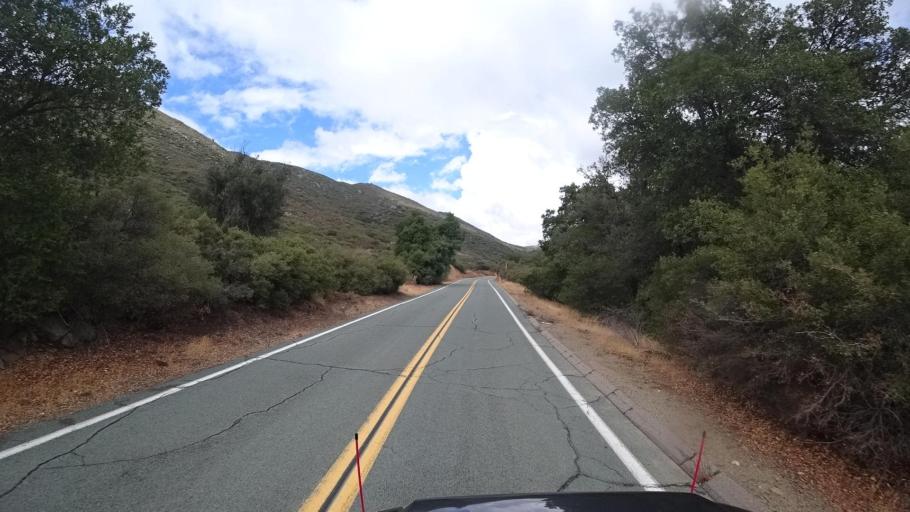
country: US
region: California
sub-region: San Diego County
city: Pine Valley
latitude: 32.7853
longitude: -116.4510
